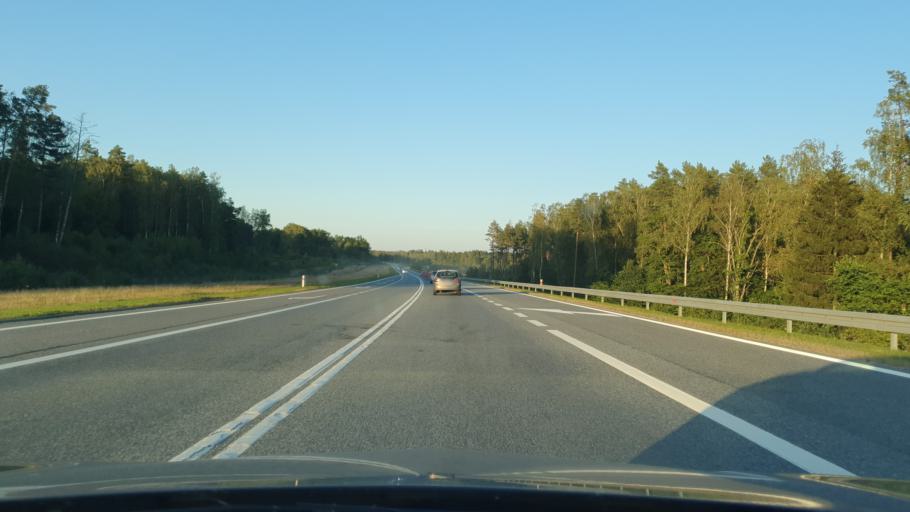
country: PL
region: Pomeranian Voivodeship
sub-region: Slupsk
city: Slupsk
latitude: 54.4338
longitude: 17.0621
